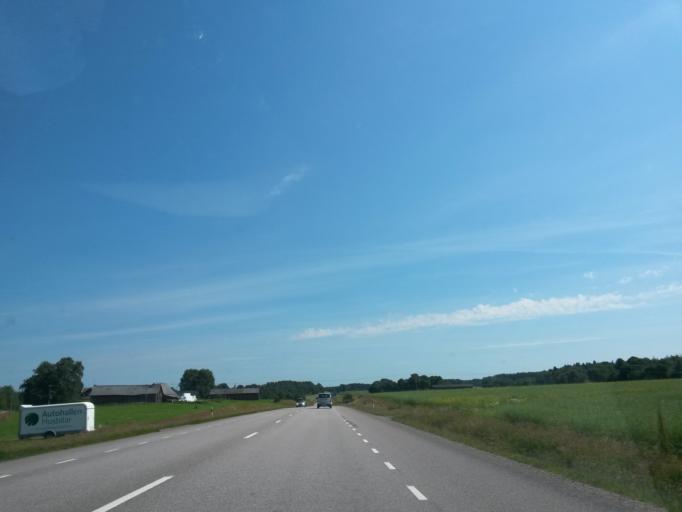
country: SE
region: Vaestra Goetaland
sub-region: Vargarda Kommun
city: Jonstorp
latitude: 57.9687
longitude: 12.6481
